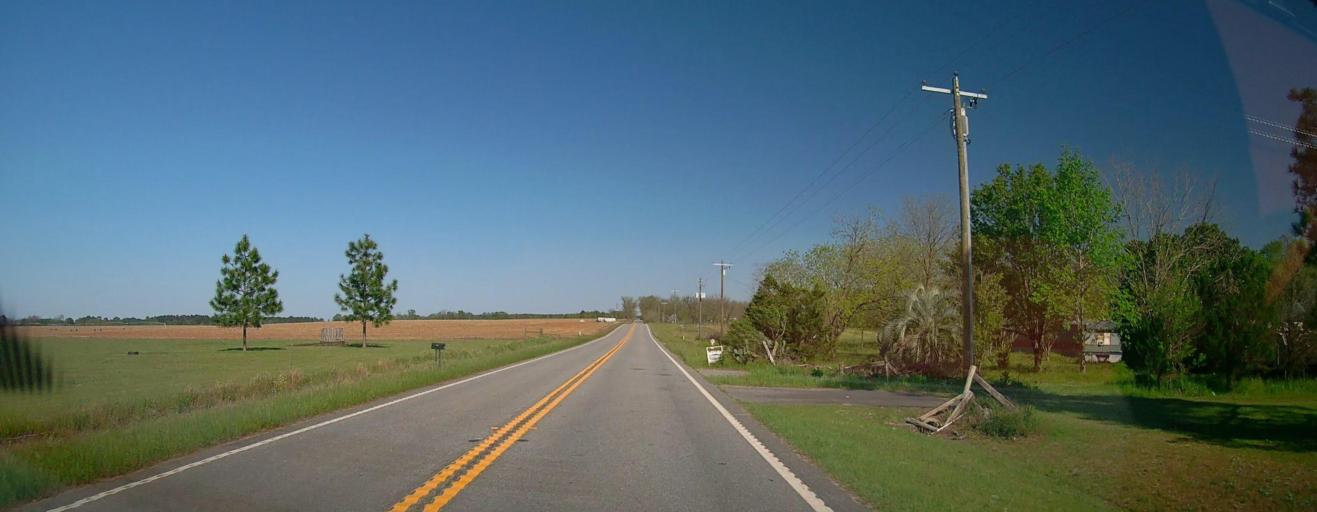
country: US
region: Georgia
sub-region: Dooly County
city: Unadilla
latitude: 32.2603
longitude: -83.7118
